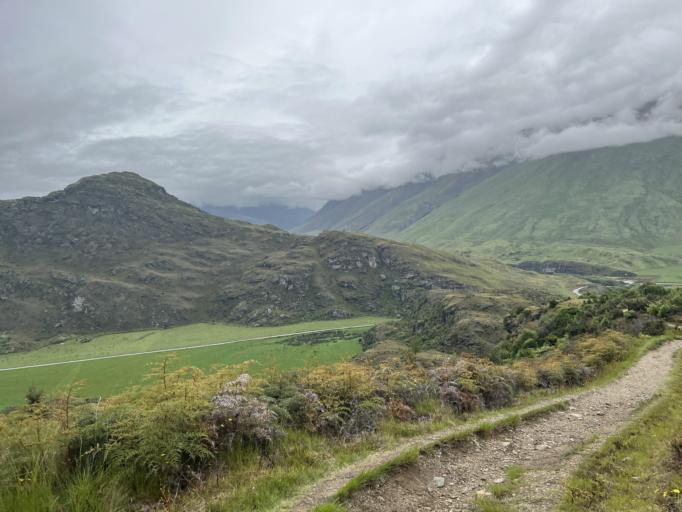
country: NZ
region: Otago
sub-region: Queenstown-Lakes District
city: Wanaka
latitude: -44.6449
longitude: 168.9687
